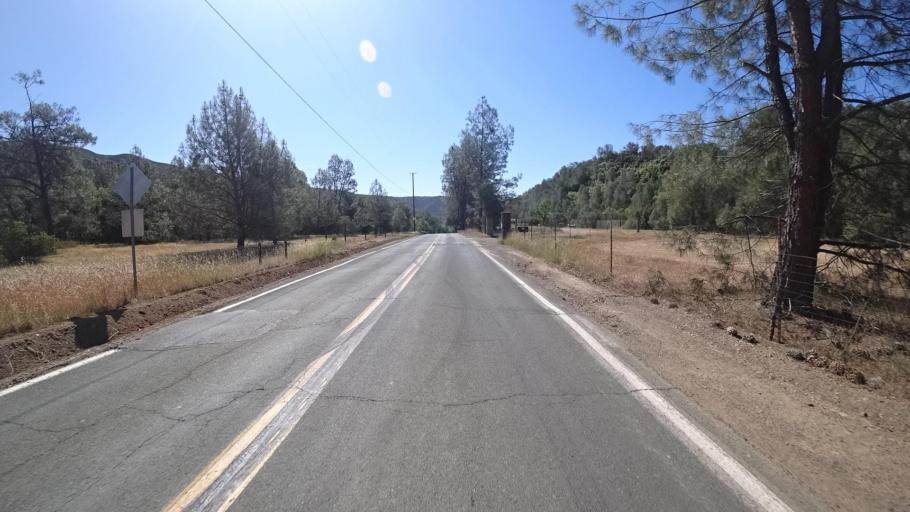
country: US
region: California
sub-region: Lake County
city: Clearlake Oaks
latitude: 39.0501
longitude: -122.5828
